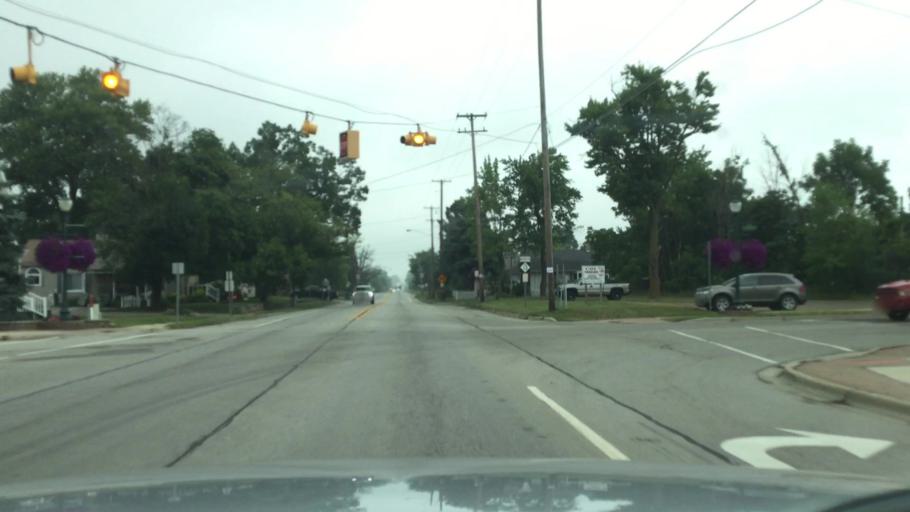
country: US
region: Michigan
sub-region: Shiawassee County
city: Durand
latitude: 42.9853
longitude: -83.9287
